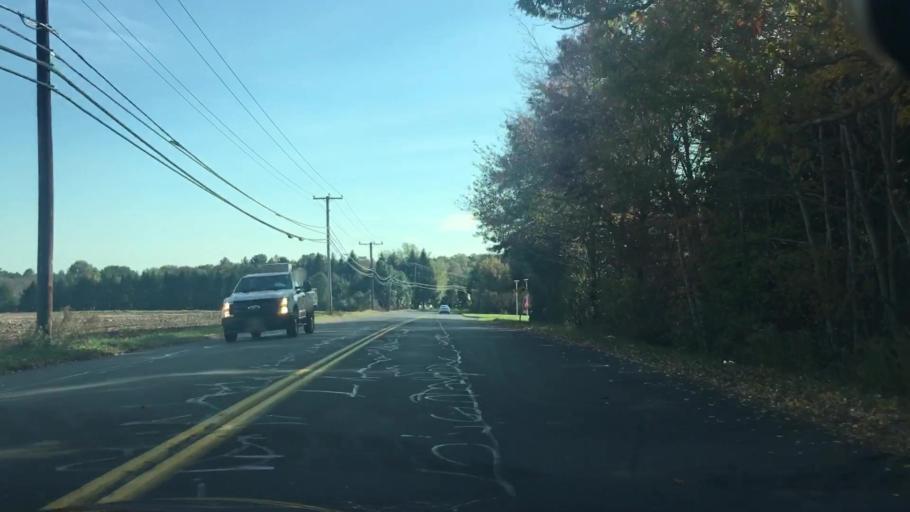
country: US
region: Connecticut
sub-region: Hartford County
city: Hazardville
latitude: 42.0105
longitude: -72.5129
